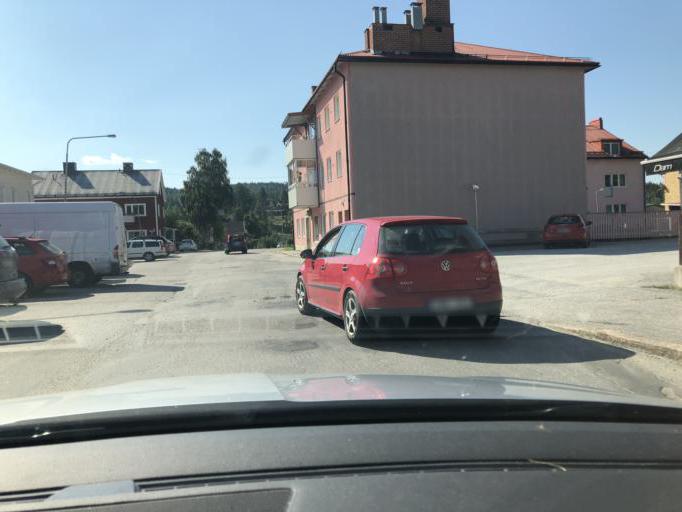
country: SE
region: Vaesternorrland
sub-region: OErnskoeldsviks Kommun
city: Bredbyn
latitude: 63.4481
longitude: 18.1088
